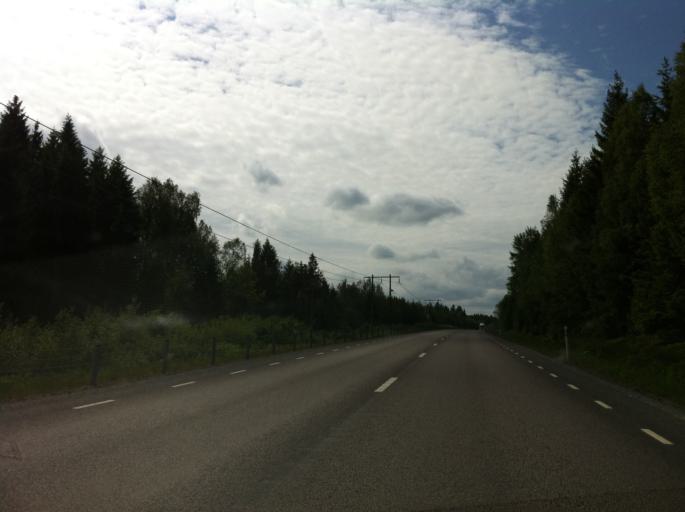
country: SE
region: Vaermland
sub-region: Karlstads Kommun
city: Edsvalla
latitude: 59.4387
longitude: 13.2022
